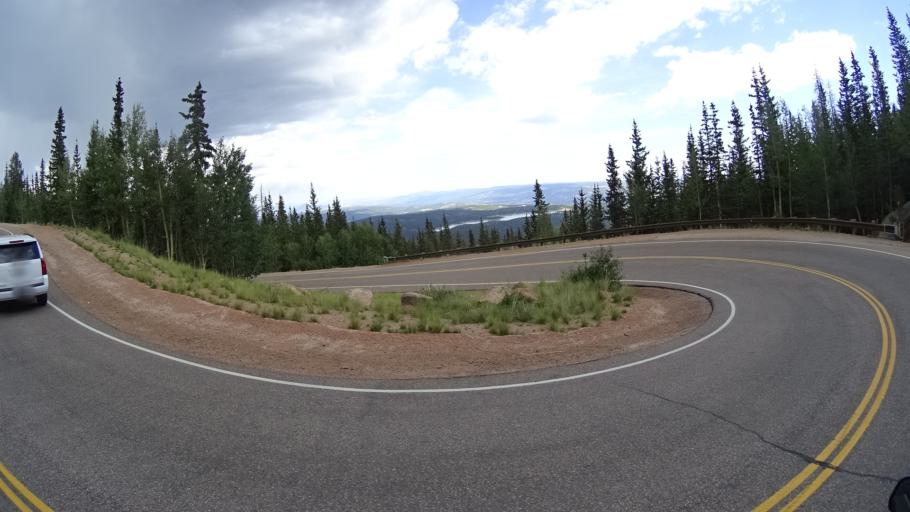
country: US
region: Colorado
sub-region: El Paso County
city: Cascade-Chipita Park
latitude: 38.8908
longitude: -105.0668
